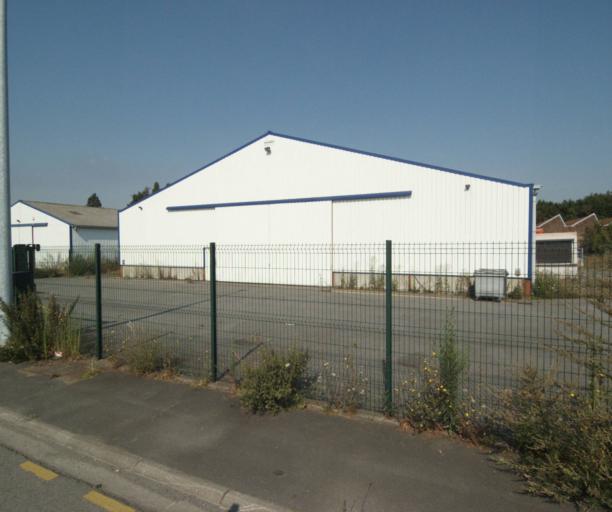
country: FR
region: Nord-Pas-de-Calais
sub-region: Departement du Nord
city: Quesnoy-sur-Deule
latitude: 50.7077
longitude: 3.0050
